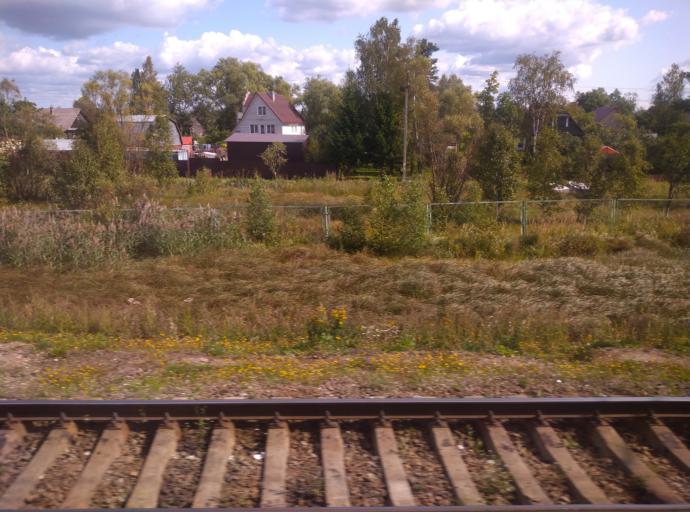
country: RU
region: Leningrad
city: Ul'yanovka
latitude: 59.6327
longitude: 30.7613
